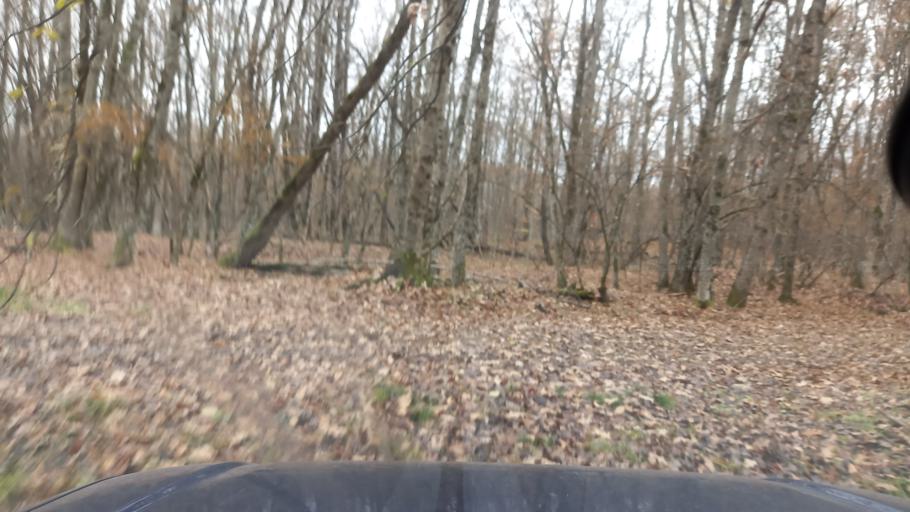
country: RU
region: Krasnodarskiy
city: Goryachiy Klyuch
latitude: 44.5062
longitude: 39.2891
